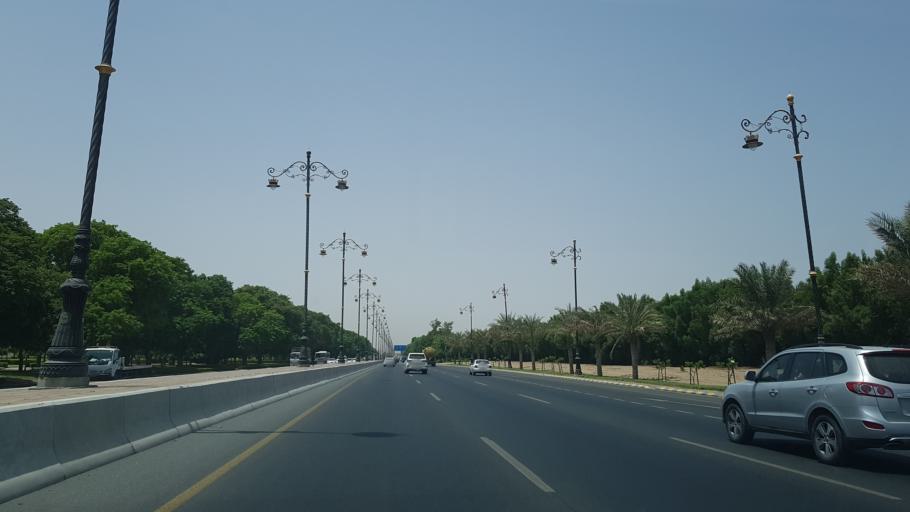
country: OM
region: Muhafazat Masqat
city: Bawshar
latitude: 23.5896
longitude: 58.3175
